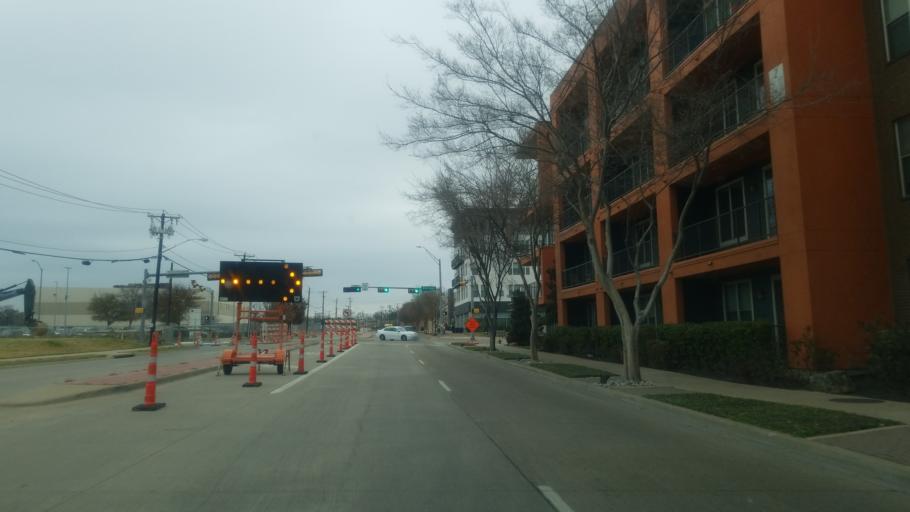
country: US
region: Texas
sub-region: Dallas County
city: Dallas
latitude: 32.8120
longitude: -96.8324
